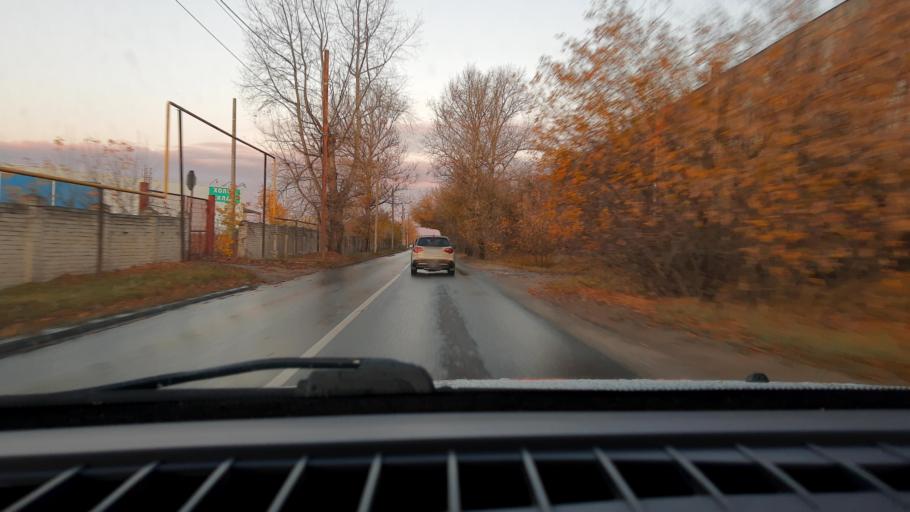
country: RU
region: Nizjnij Novgorod
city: Gorbatovka
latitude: 56.3466
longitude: 43.8222
